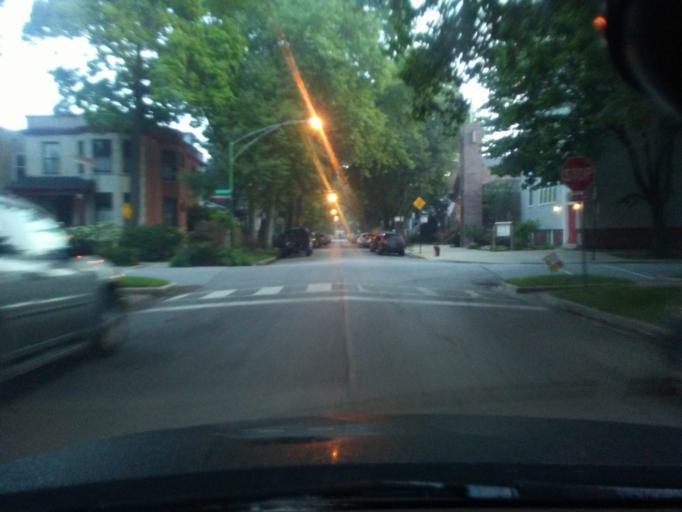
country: US
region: Illinois
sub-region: Cook County
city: Lincolnwood
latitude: 41.9522
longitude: -87.6702
